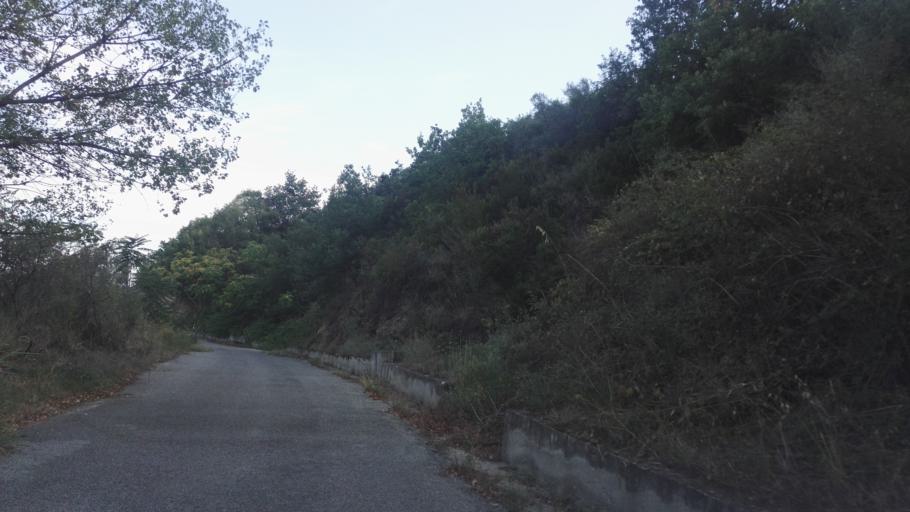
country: IT
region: Calabria
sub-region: Provincia di Reggio Calabria
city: Camini
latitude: 38.4341
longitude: 16.4800
